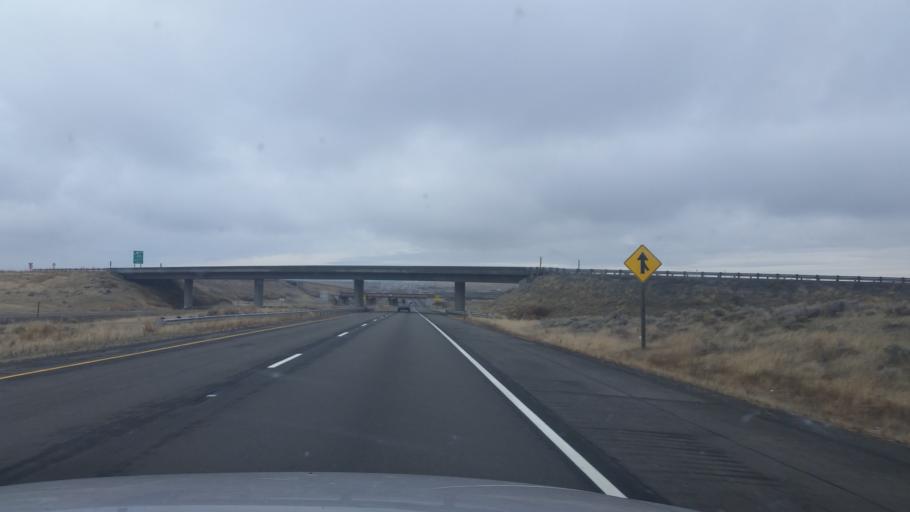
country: US
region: Washington
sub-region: Adams County
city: Ritzville
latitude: 47.1115
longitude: -118.3933
